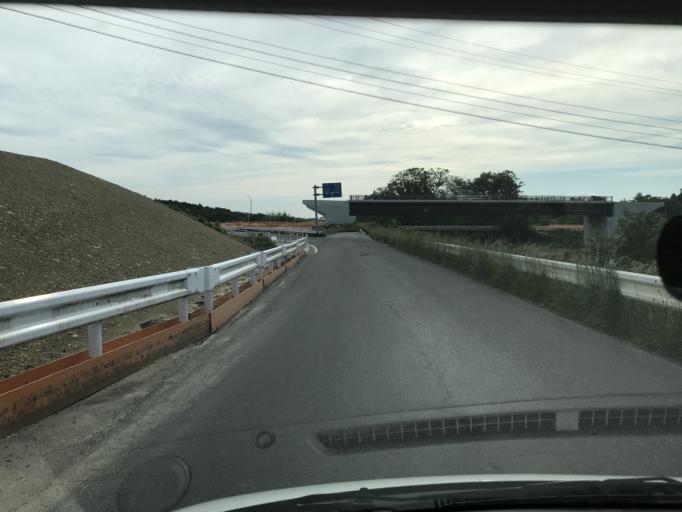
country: JP
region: Miyagi
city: Wakuya
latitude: 38.6549
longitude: 141.2895
